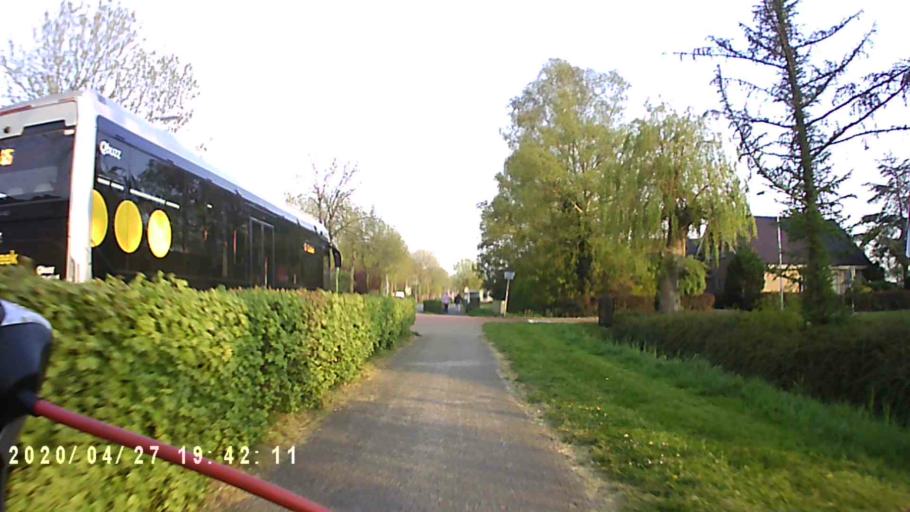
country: NL
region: Groningen
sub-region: Gemeente Winsum
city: Winsum
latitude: 53.3598
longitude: 6.4626
